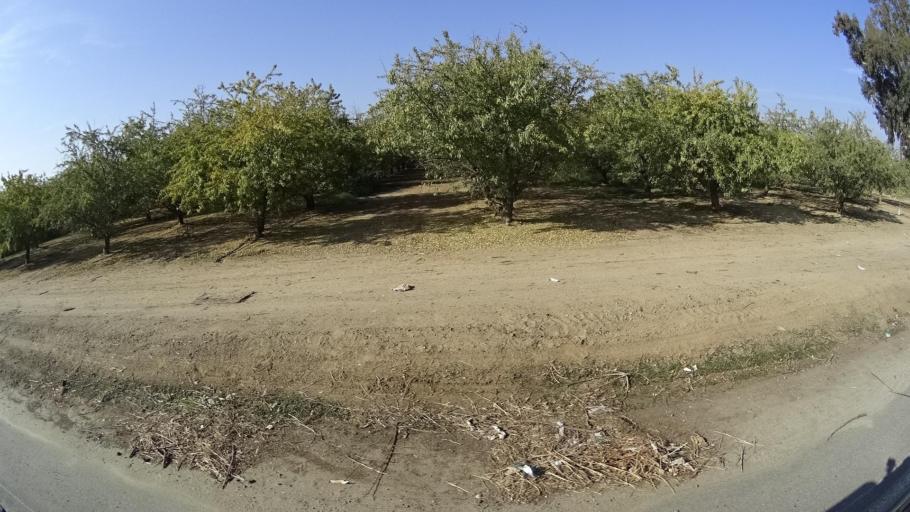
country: US
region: California
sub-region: Kern County
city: McFarland
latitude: 35.6879
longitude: -119.2231
